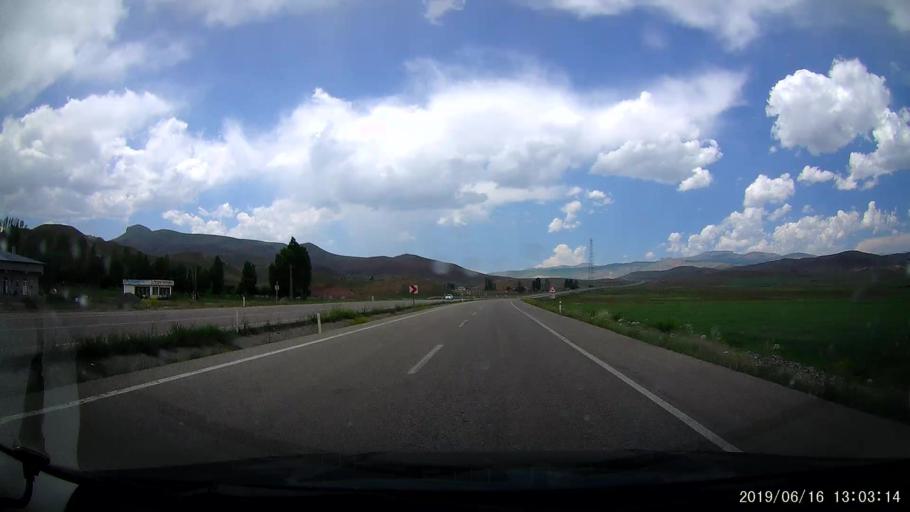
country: TR
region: Agri
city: Sulucem
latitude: 39.5795
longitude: 43.7948
